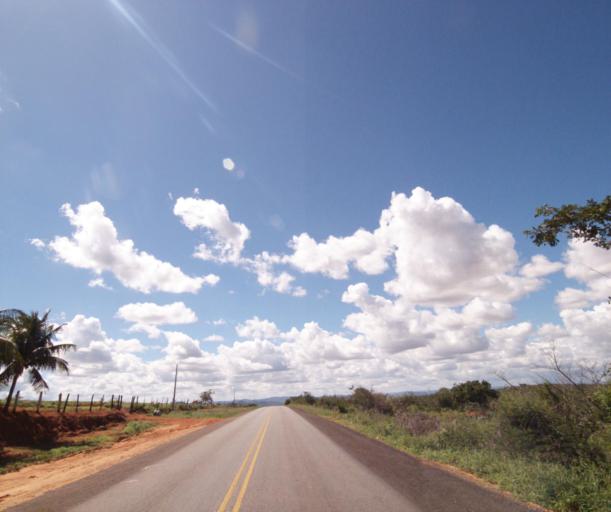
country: BR
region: Bahia
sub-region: Cacule
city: Cacule
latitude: -14.1892
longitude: -42.1592
